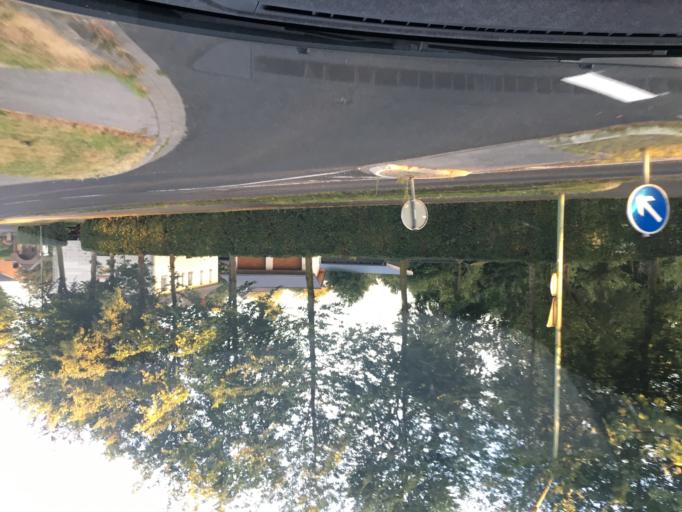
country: DE
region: North Rhine-Westphalia
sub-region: Regierungsbezirk Koln
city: Simmerath
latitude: 50.6341
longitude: 6.3196
